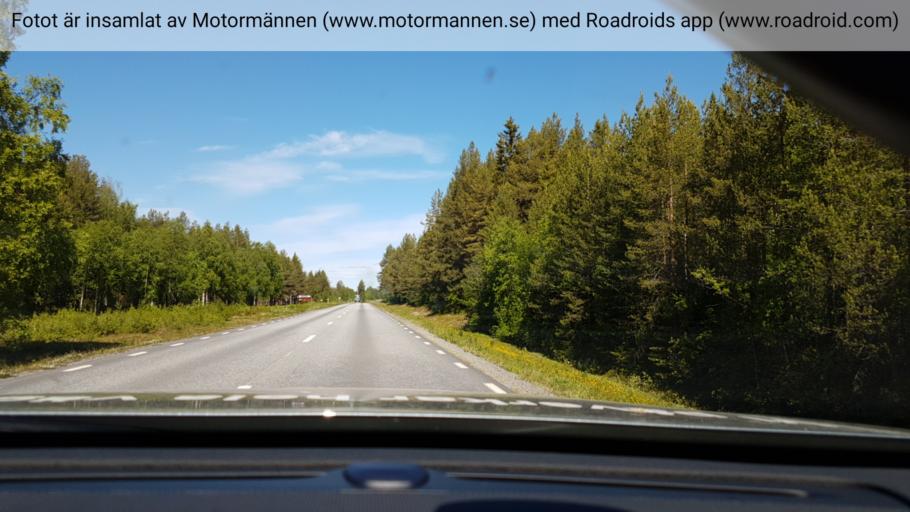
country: SE
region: Vaesterbotten
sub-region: Vilhelmina Kommun
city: Vilhelmina
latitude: 64.4733
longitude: 16.7937
